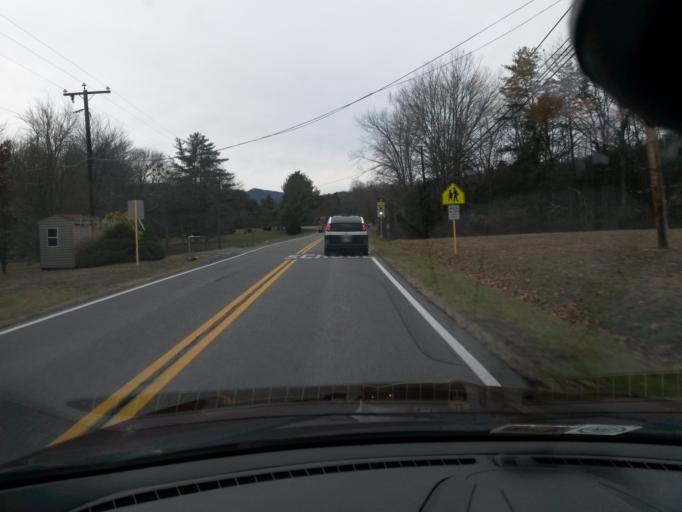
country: US
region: Virginia
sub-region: Alleghany County
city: Clifton Forge
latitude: 37.8122
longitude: -79.7430
